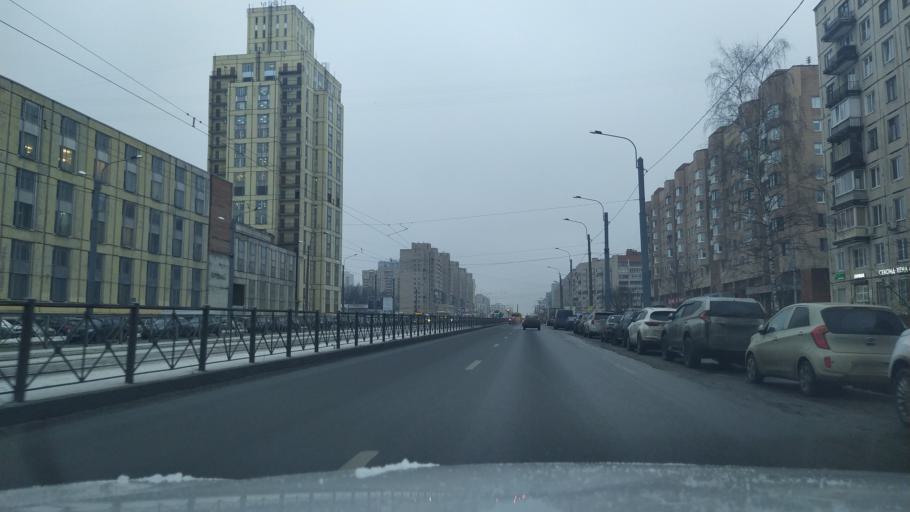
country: RU
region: St.-Petersburg
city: Grazhdanka
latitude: 60.0347
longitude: 30.4244
